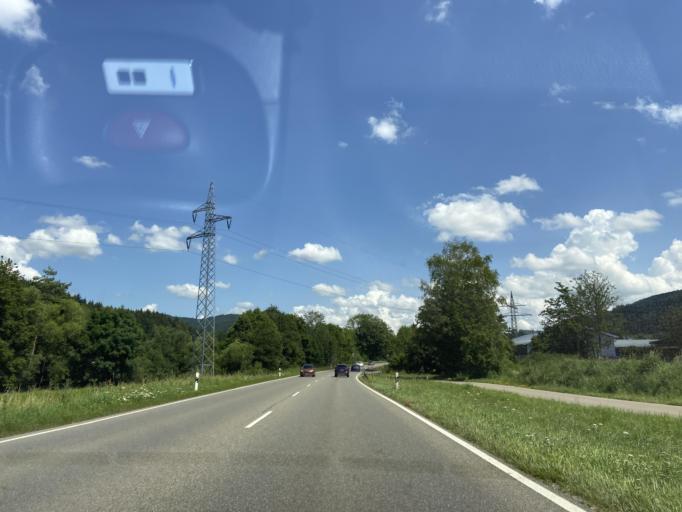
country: DE
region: Baden-Wuerttemberg
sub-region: Tuebingen Region
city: Messstetten
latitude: 48.2147
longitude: 8.9390
